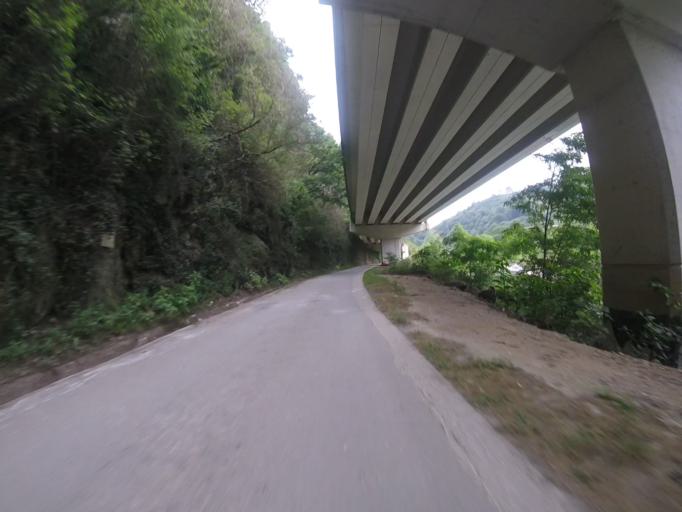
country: ES
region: Navarre
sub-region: Provincia de Navarra
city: Sunbilla
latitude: 43.1802
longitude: -1.6709
